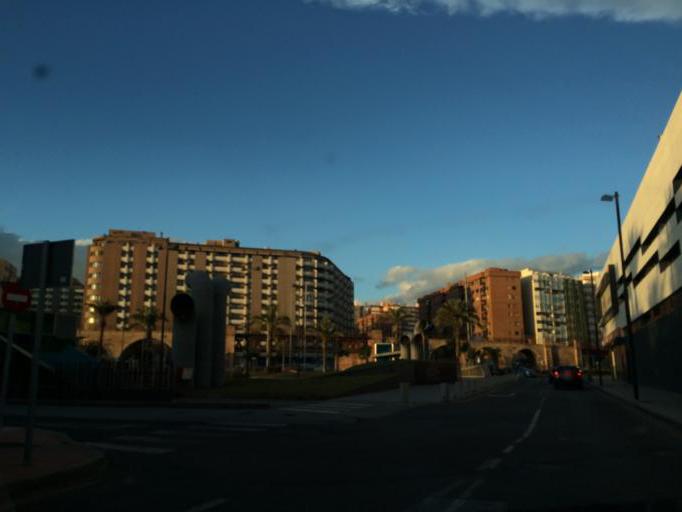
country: ES
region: Andalusia
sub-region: Provincia de Almeria
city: Almeria
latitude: 36.8322
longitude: -2.4606
